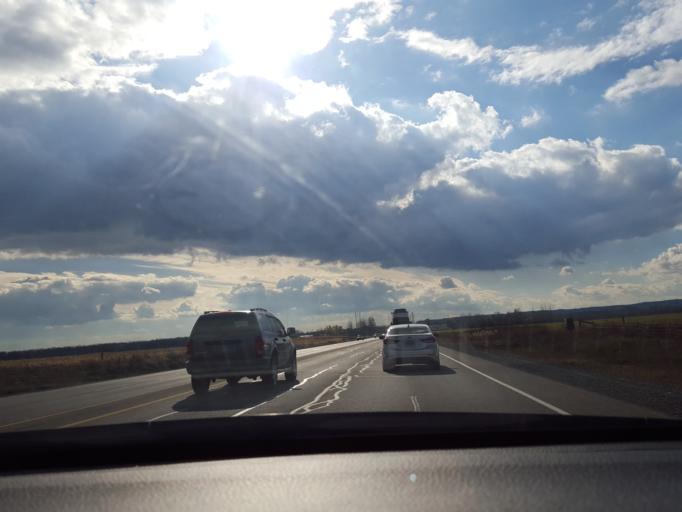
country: CA
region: Ontario
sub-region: Halton
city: Milton
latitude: 43.5606
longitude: -79.8022
